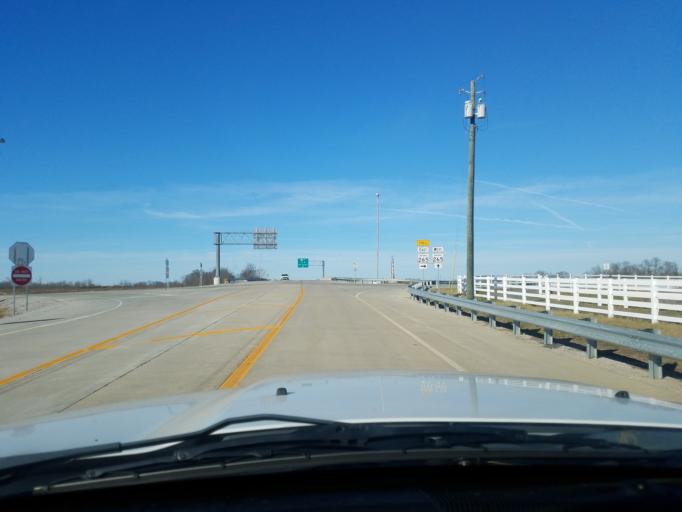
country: US
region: Kentucky
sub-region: Jefferson County
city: Prospect
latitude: 38.3480
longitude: -85.6667
